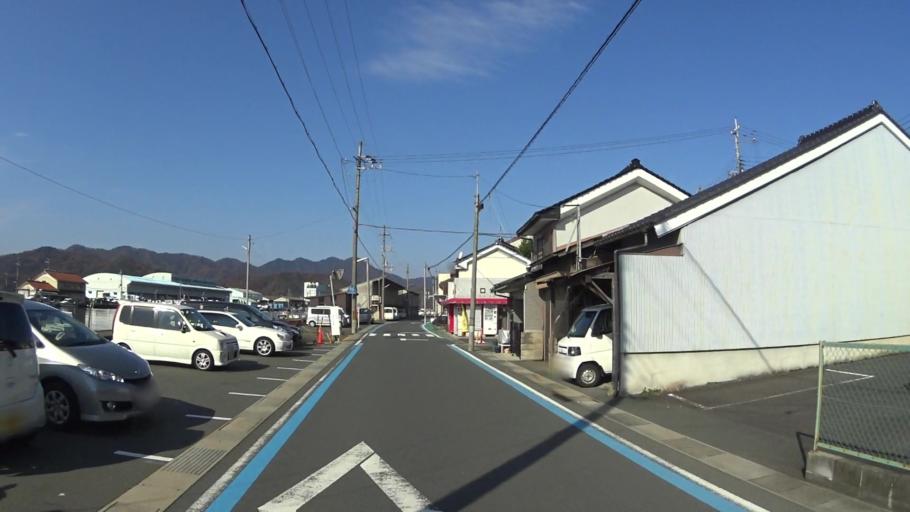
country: JP
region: Kyoto
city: Maizuru
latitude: 35.4559
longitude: 135.3282
